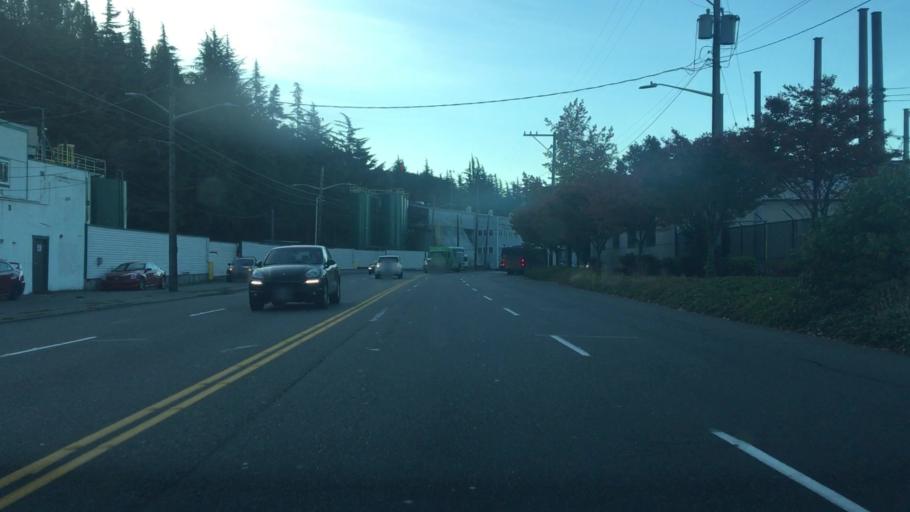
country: US
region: Washington
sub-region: King County
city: Seattle
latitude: 47.5892
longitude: -122.3219
